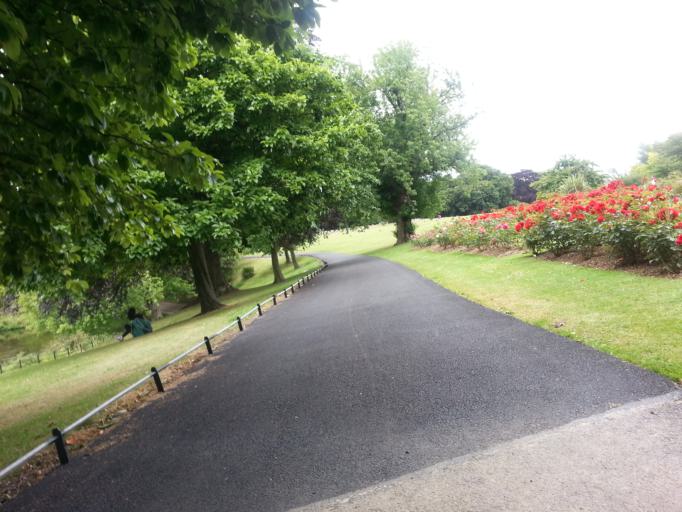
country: IE
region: Leinster
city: Rialto
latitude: 53.3511
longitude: -6.3015
